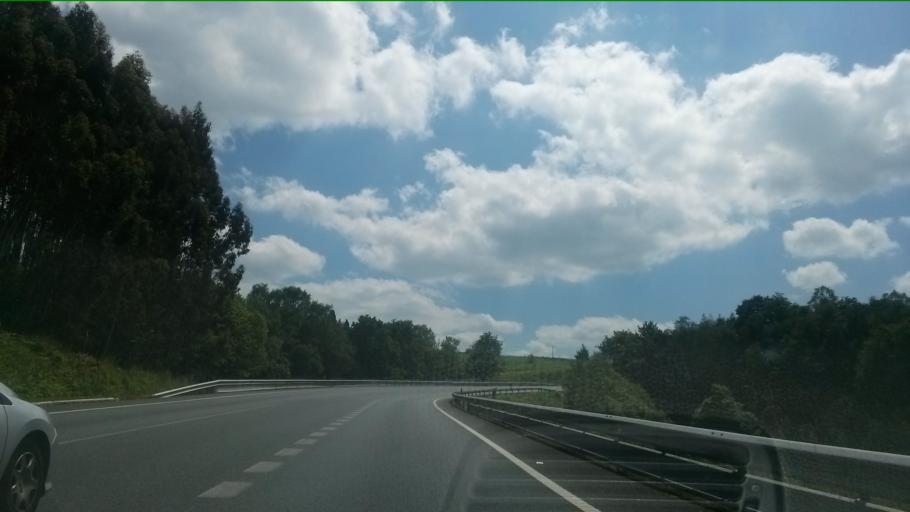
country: ES
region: Galicia
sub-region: Provincia da Coruna
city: Frades
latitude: 43.0144
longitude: -8.2590
